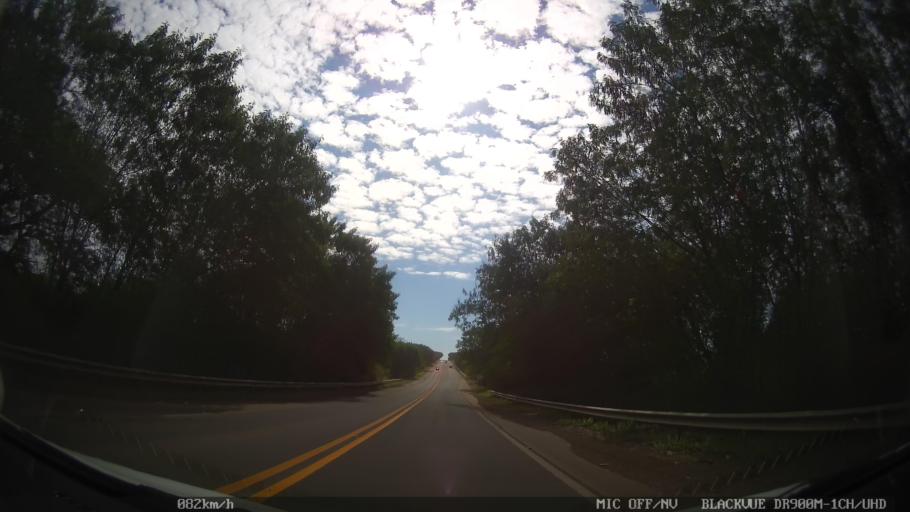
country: BR
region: Sao Paulo
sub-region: Santa Barbara D'Oeste
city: Santa Barbara d'Oeste
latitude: -22.7331
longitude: -47.4240
